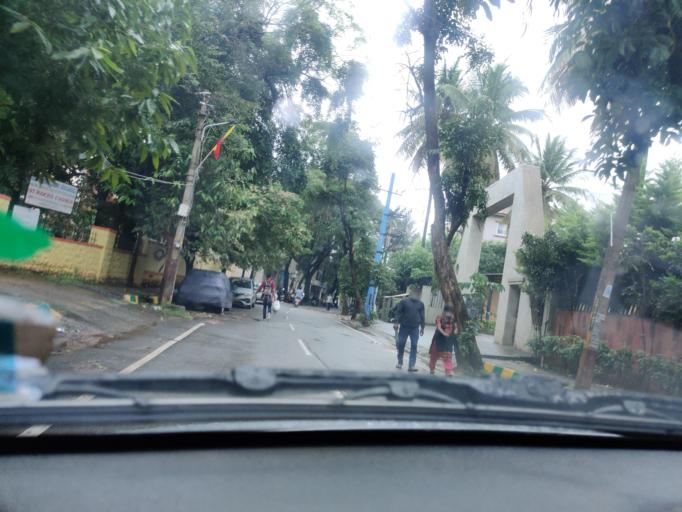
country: IN
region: Karnataka
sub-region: Bangalore Urban
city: Bangalore
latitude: 13.0281
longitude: 77.6381
